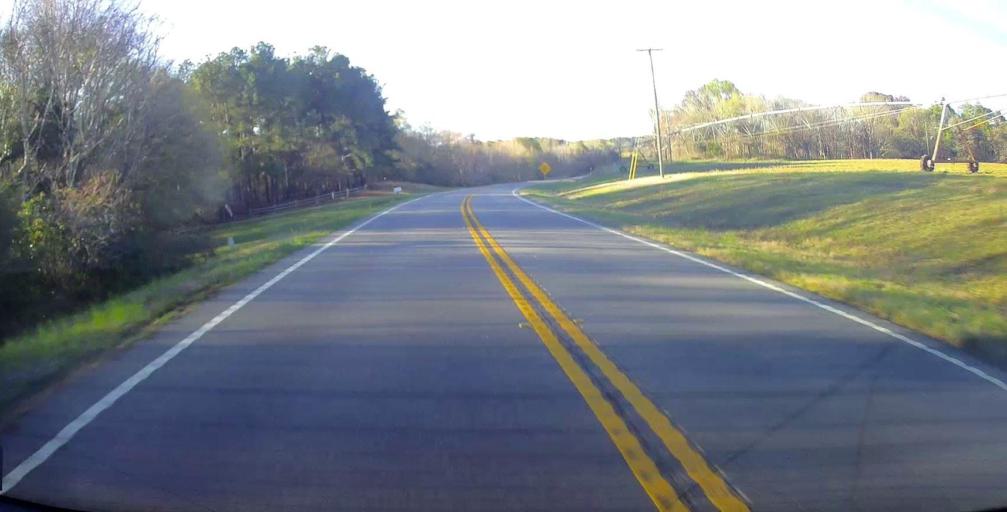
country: US
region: Georgia
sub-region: Pulaski County
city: Hawkinsville
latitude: 32.2471
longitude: -83.4101
